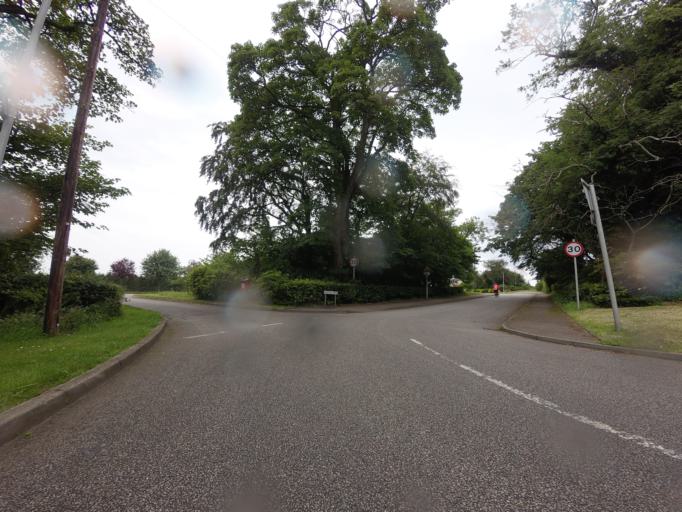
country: GB
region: Scotland
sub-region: Moray
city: Cullen
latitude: 57.6838
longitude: -2.8143
